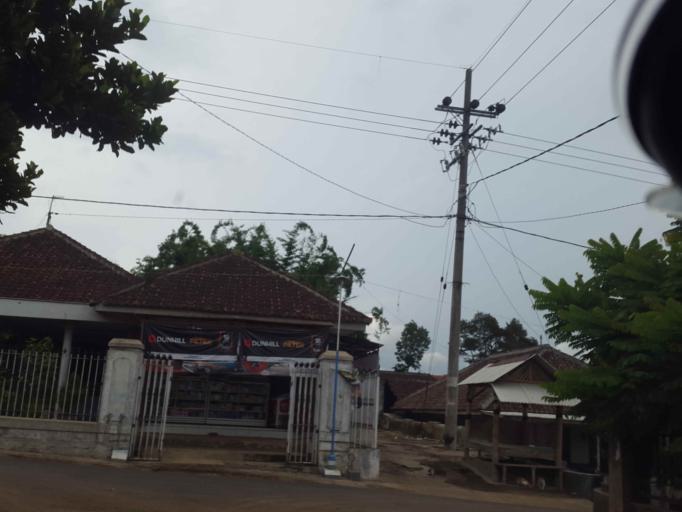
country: ID
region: East Java
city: Niwen
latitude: -7.9530
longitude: 112.5718
